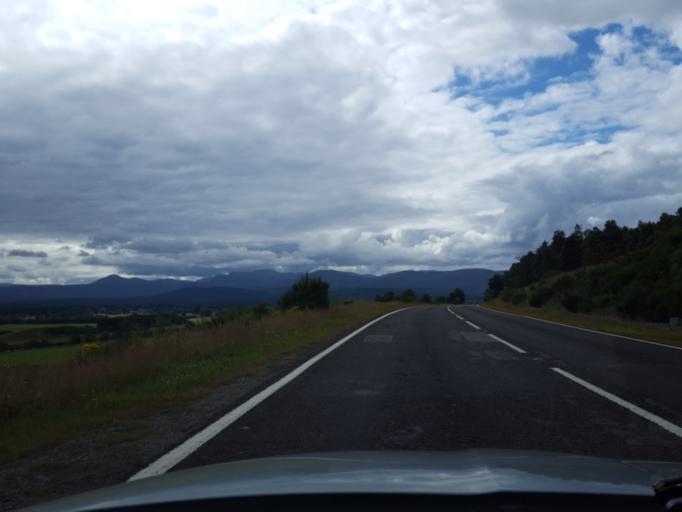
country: GB
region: Scotland
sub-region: Highland
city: Grantown on Spey
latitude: 57.2890
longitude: -3.6667
